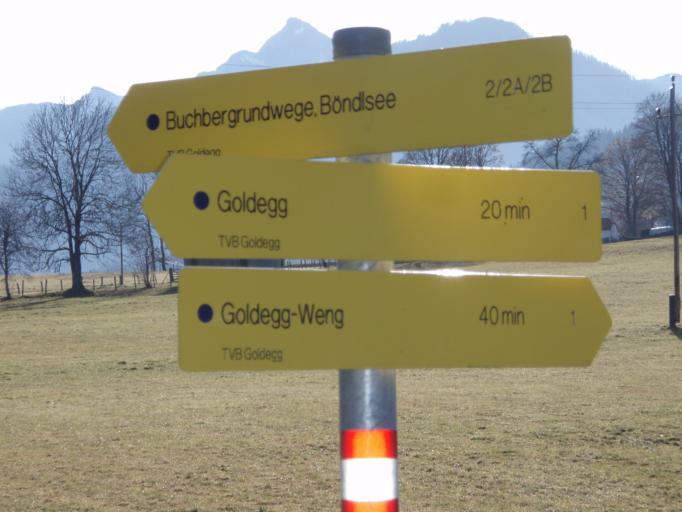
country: AT
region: Salzburg
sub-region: Politischer Bezirk Sankt Johann im Pongau
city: Goldegg
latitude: 47.3219
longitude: 13.0836
